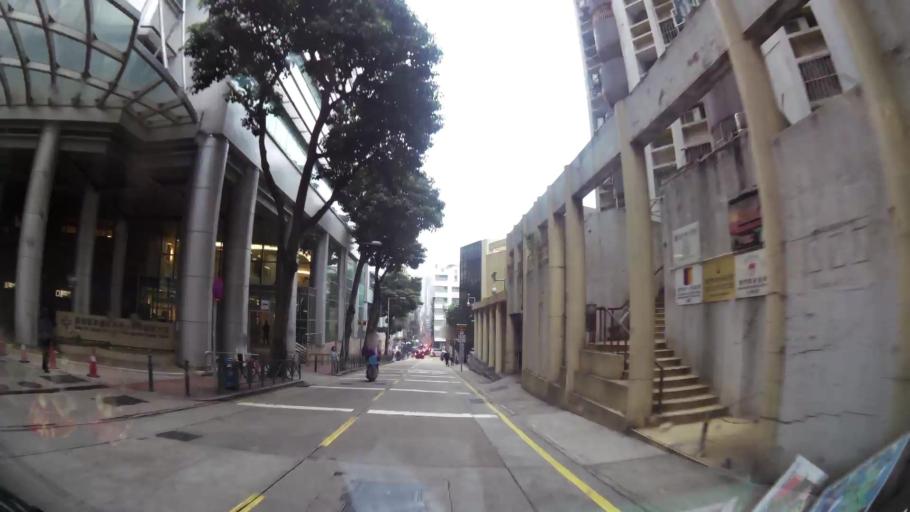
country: MO
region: Macau
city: Macau
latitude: 22.1992
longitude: 113.5435
